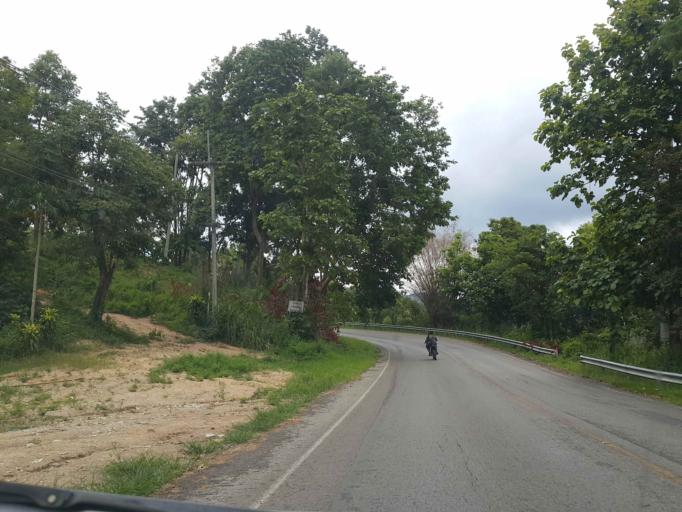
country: TH
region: Chiang Mai
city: Samoeng
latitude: 18.7997
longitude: 98.8321
